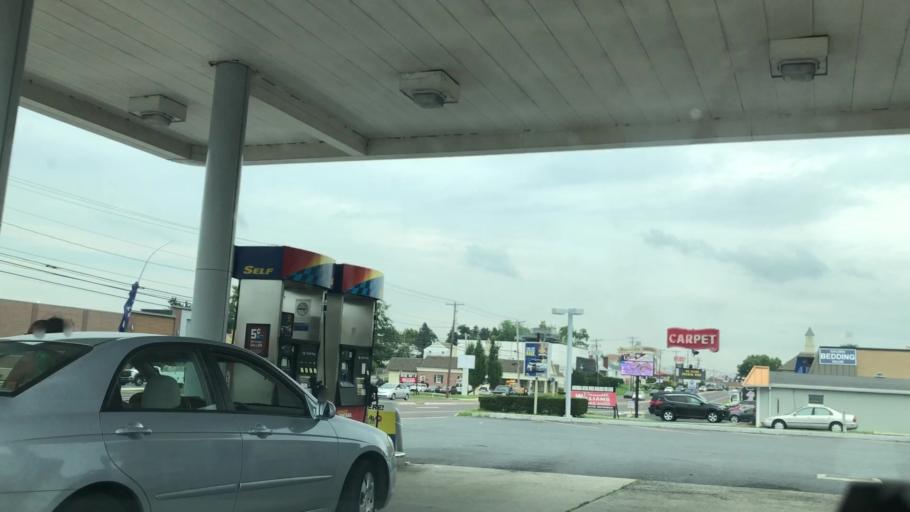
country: US
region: Pennsylvania
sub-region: Dauphin County
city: Colonial Park
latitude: 40.3029
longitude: -76.8104
